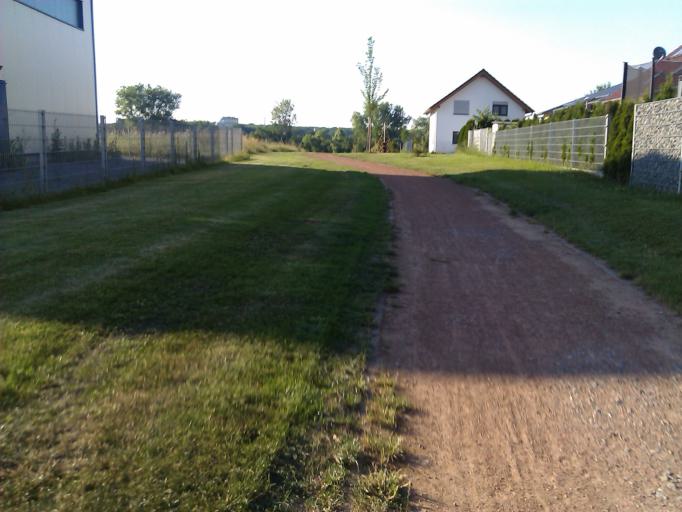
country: DE
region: Baden-Wuerttemberg
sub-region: Regierungsbezirk Stuttgart
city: Untereisesheim
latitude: 49.2218
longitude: 9.2117
